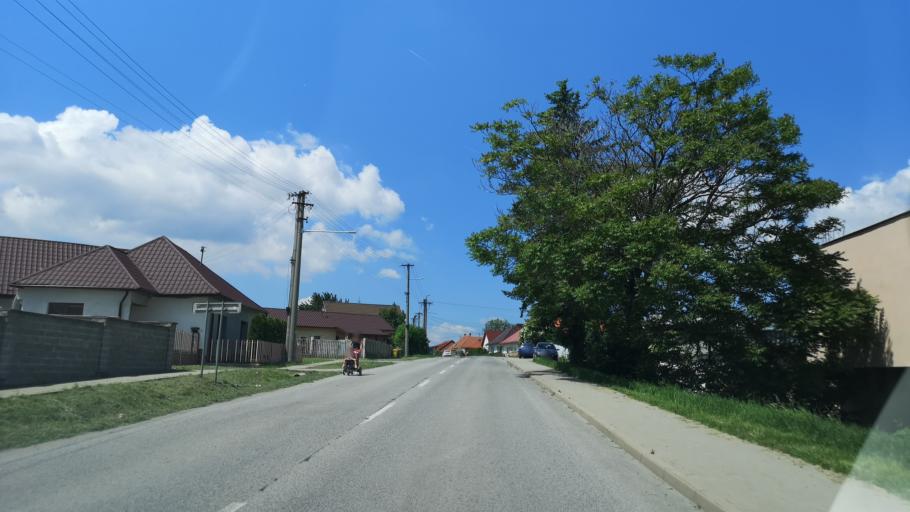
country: SK
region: Nitriansky
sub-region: Okres Nitra
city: Nitra
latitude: 48.3080
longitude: 17.9376
